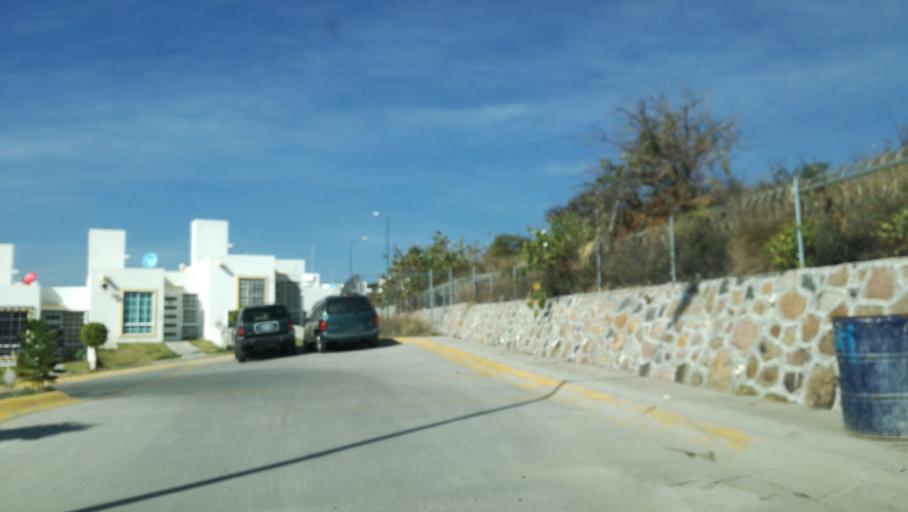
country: MX
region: Guanajuato
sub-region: Leon
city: La Ermita
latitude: 21.1606
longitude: -101.7406
